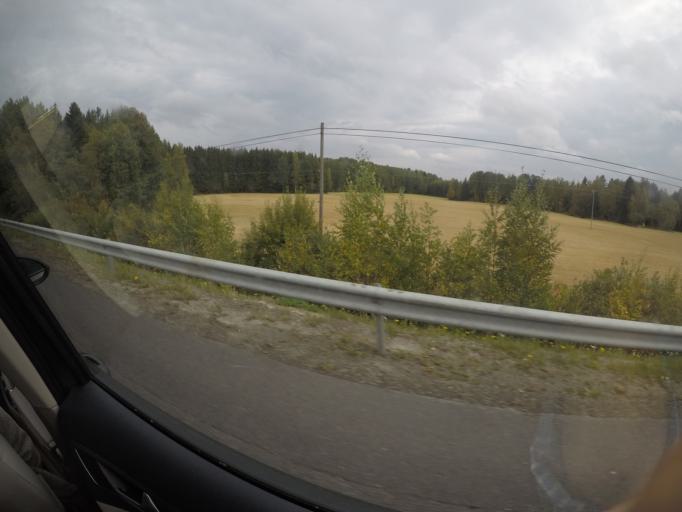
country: FI
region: Haeme
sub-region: Haemeenlinna
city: Parola
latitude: 61.0795
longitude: 24.3943
